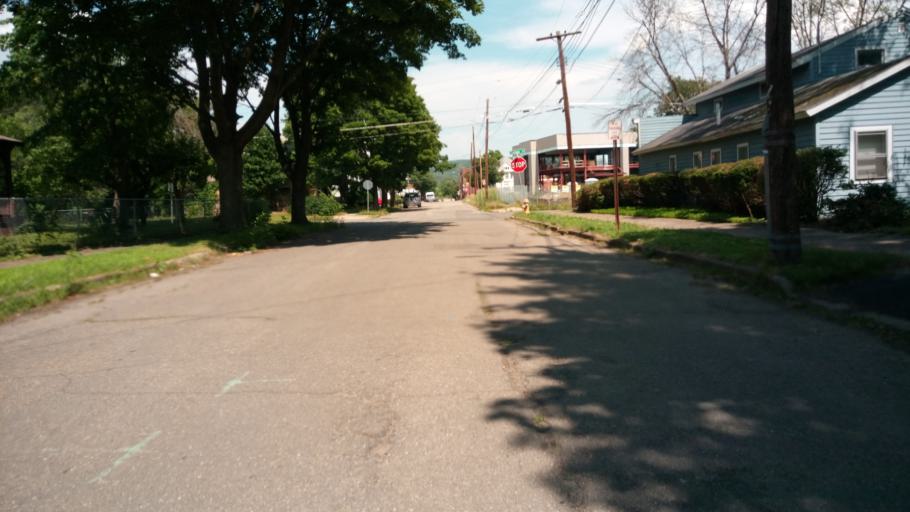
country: US
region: New York
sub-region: Chemung County
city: Elmira
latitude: 42.0941
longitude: -76.8135
